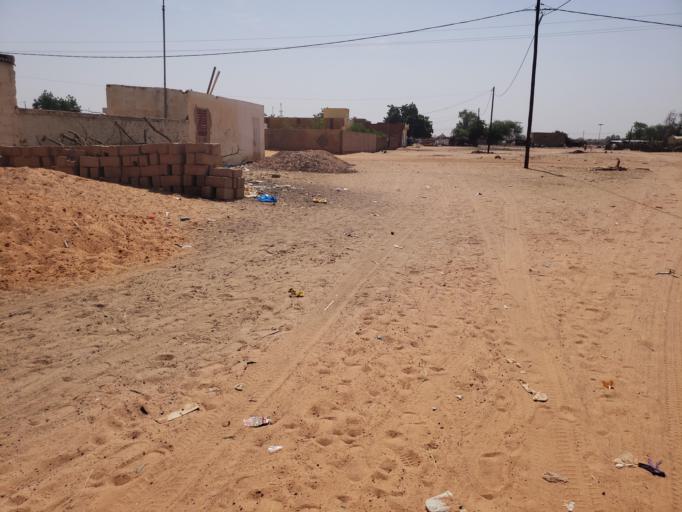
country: SN
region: Matam
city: Ranerou
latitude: 15.3000
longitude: -13.9618
